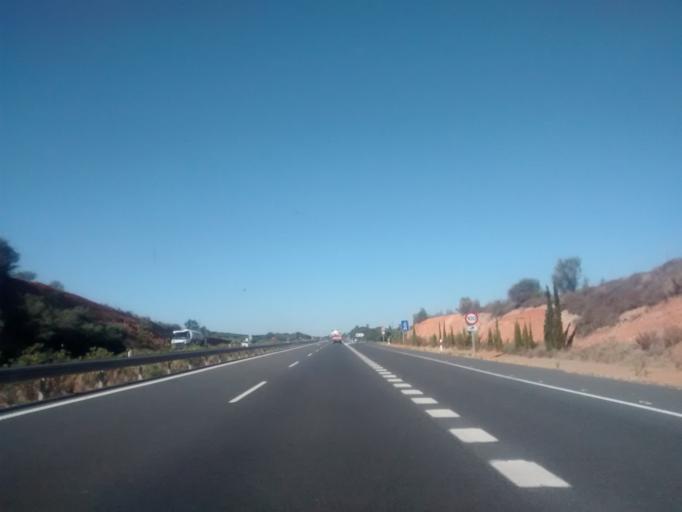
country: ES
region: Andalusia
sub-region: Provincia de Huelva
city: Villablanca
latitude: 37.2527
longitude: -7.3338
